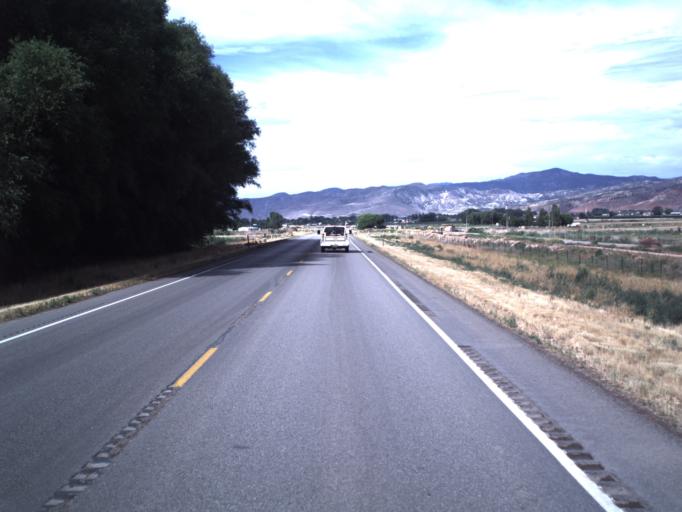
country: US
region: Utah
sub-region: Sevier County
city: Richfield
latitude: 38.7875
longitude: -112.0505
